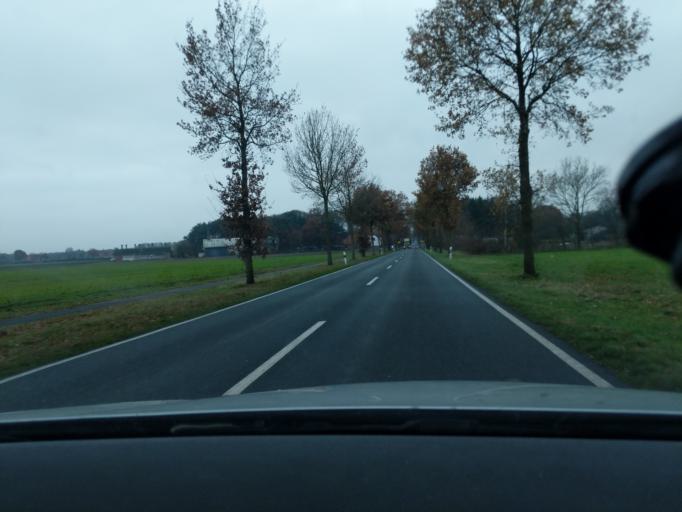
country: DE
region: Lower Saxony
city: Heeslingen
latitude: 53.3244
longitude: 9.3493
